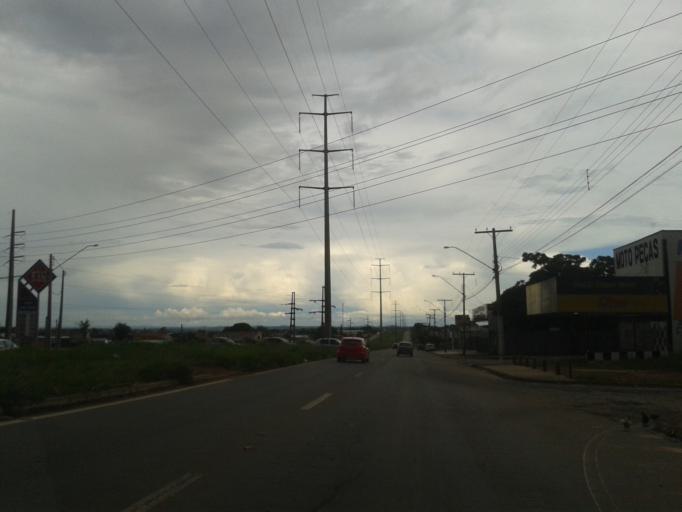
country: BR
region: Goias
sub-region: Aparecida De Goiania
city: Aparecida de Goiania
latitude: -16.7787
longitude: -49.2919
